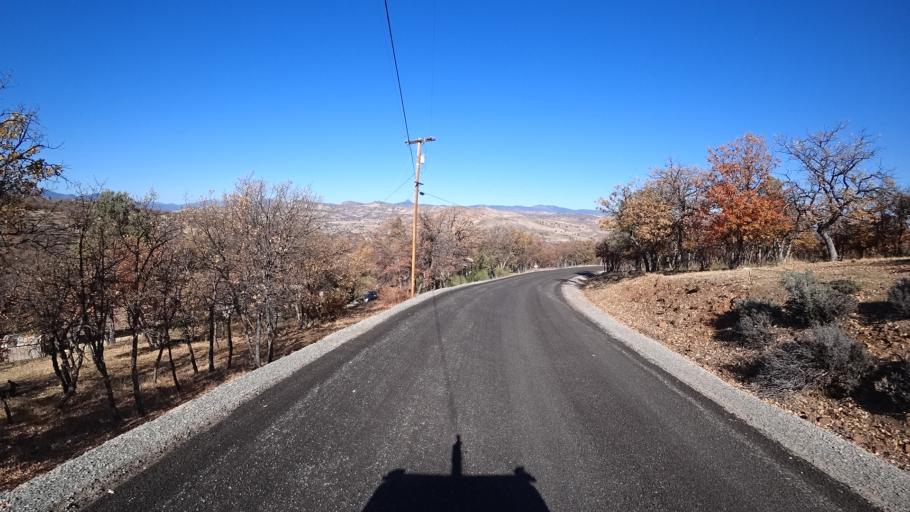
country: US
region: California
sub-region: Siskiyou County
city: Montague
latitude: 41.8817
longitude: -122.4900
